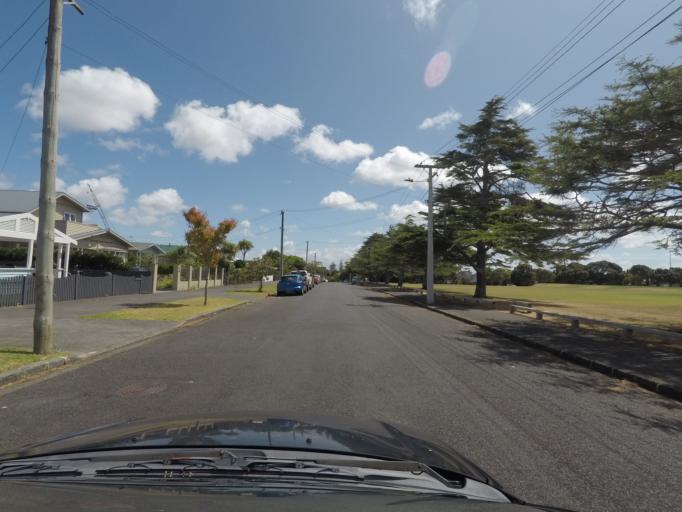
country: NZ
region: Auckland
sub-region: Auckland
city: Rosebank
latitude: -36.8655
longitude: 174.7023
